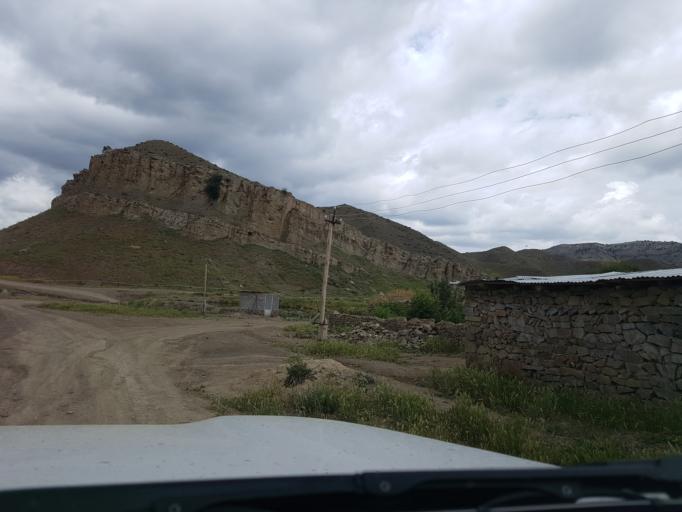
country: TM
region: Ahal
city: Baharly
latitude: 38.2011
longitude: 57.0050
